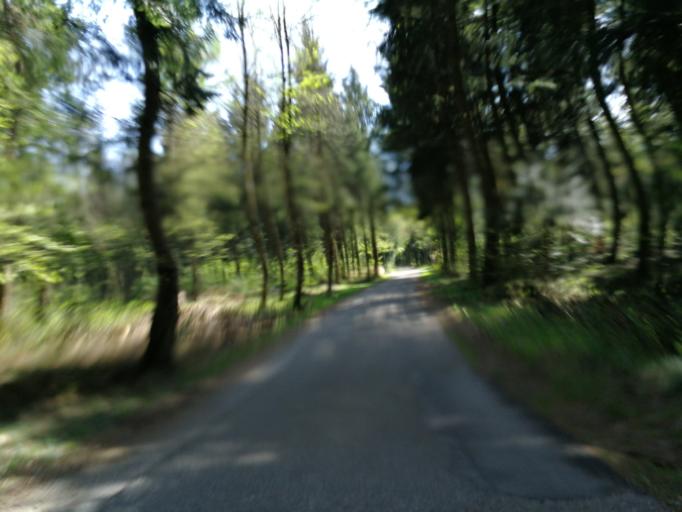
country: CH
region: Zurich
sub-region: Bezirk Hinwil
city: Hinwil
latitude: 47.3005
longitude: 8.8199
